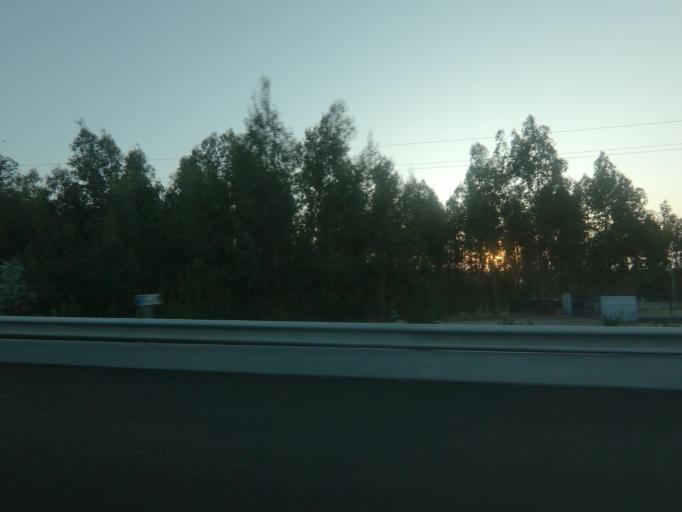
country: PT
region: Leiria
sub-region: Pombal
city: Pombal
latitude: 39.8978
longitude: -8.6904
